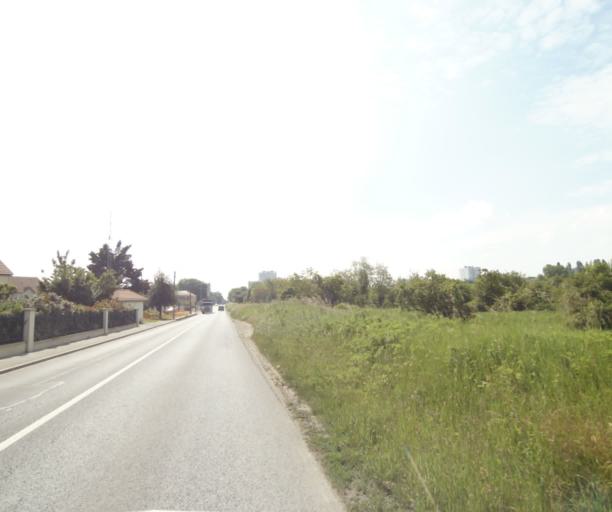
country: FR
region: Ile-de-France
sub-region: Departement du Val-d'Oise
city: Sannois
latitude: 48.9588
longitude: 2.2278
